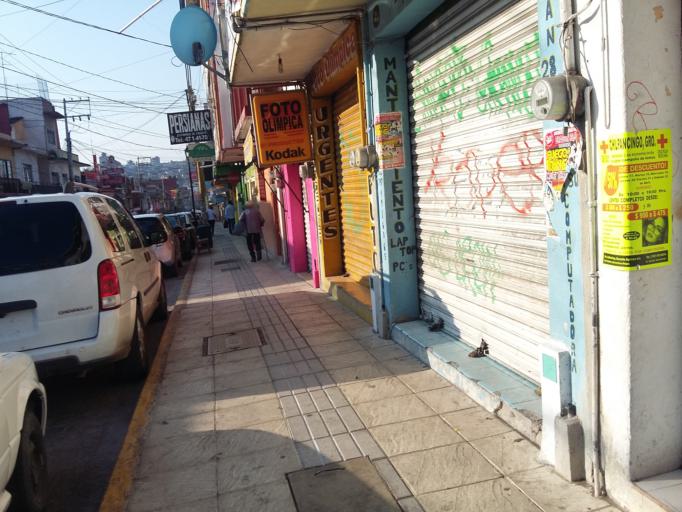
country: MX
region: Guerrero
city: Chilpancingo de los Bravos
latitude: 17.5501
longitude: -99.5003
